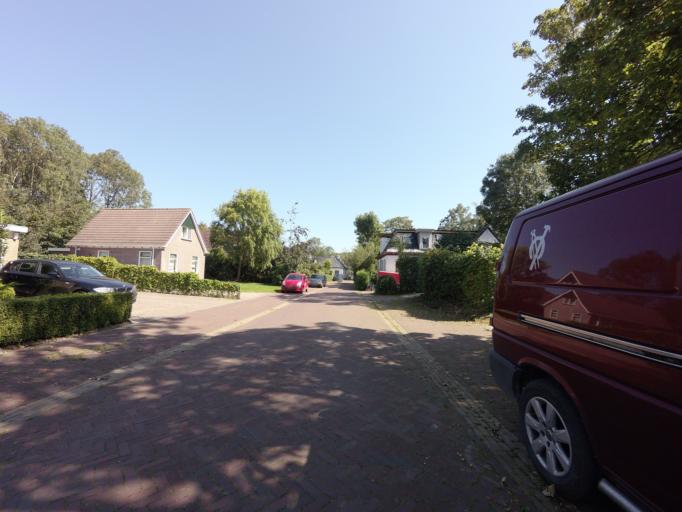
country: NL
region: Friesland
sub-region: Gemeente Dongeradeel
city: Ternaard
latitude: 53.3726
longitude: 5.9966
